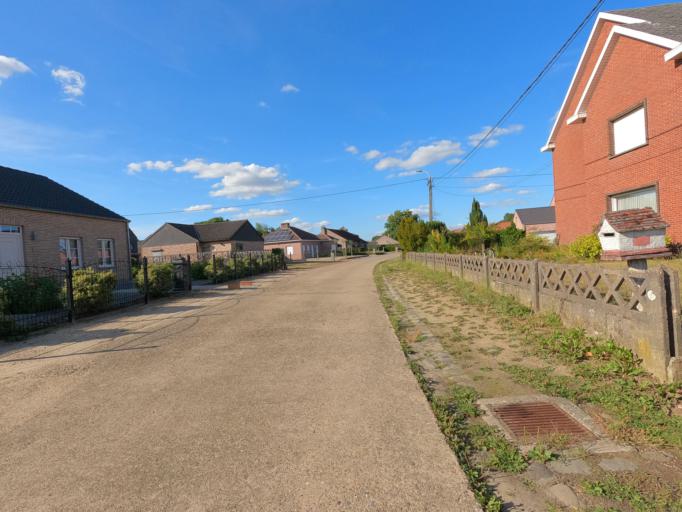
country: BE
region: Flanders
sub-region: Provincie Antwerpen
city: Hulshout
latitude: 51.0677
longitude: 4.8215
